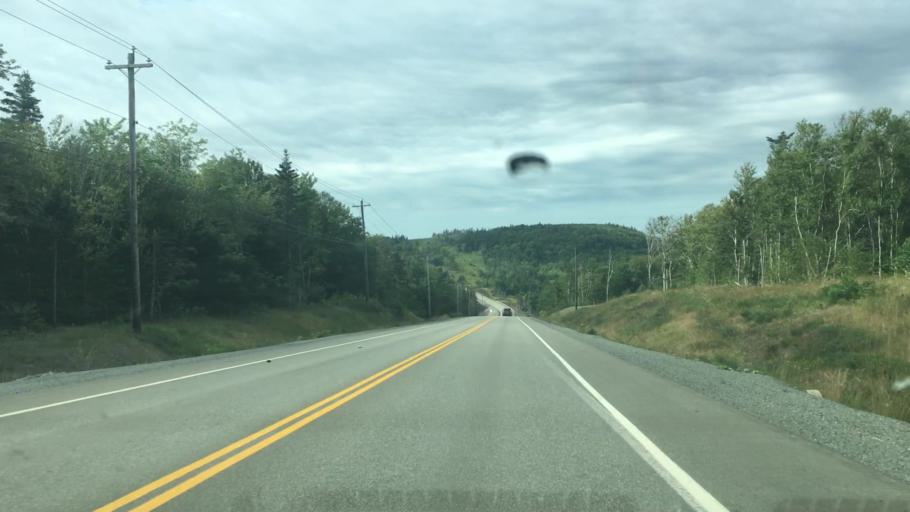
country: CA
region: Nova Scotia
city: Princeville
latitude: 45.6696
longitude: -60.8033
